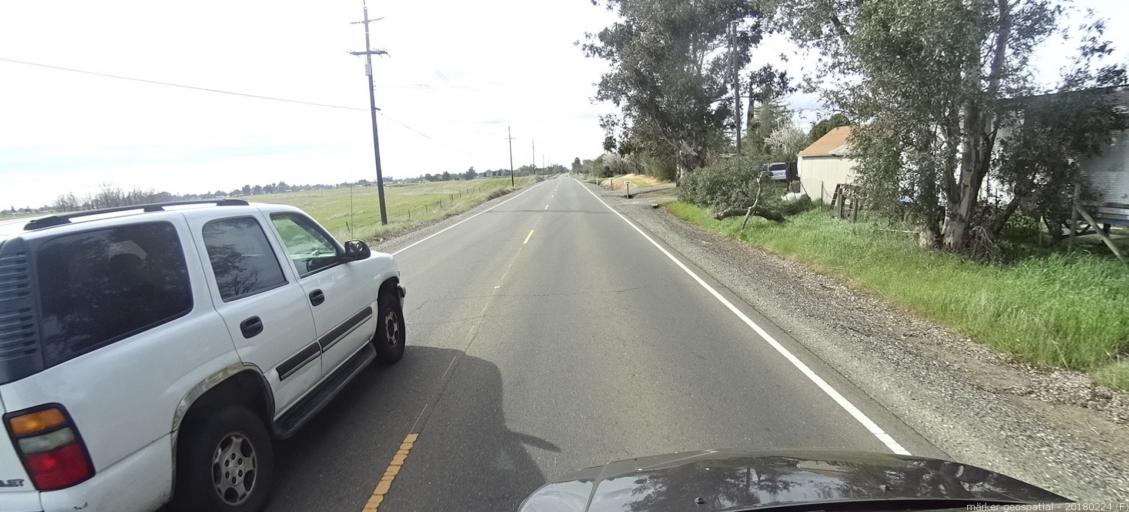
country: US
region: California
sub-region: Sacramento County
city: Rio Linda
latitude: 38.7144
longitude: -121.4322
